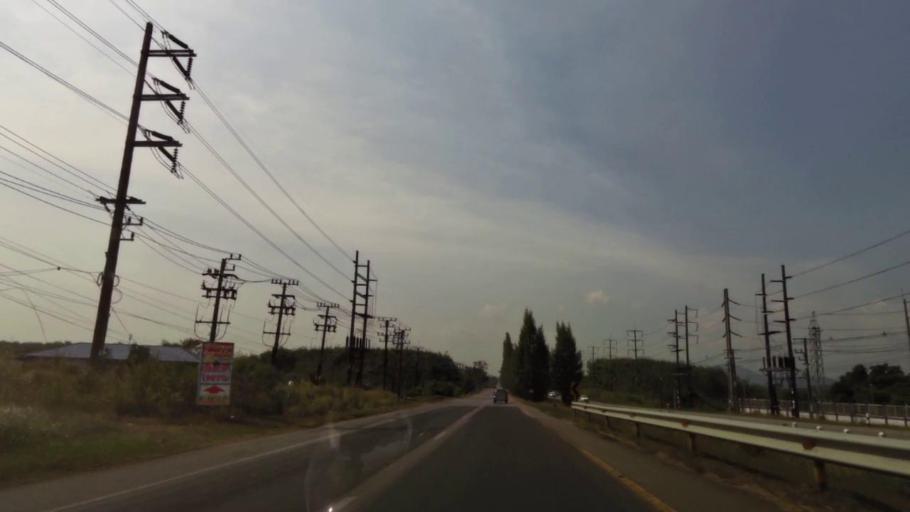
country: TH
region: Chanthaburi
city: Chanthaburi
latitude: 12.6633
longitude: 102.1185
